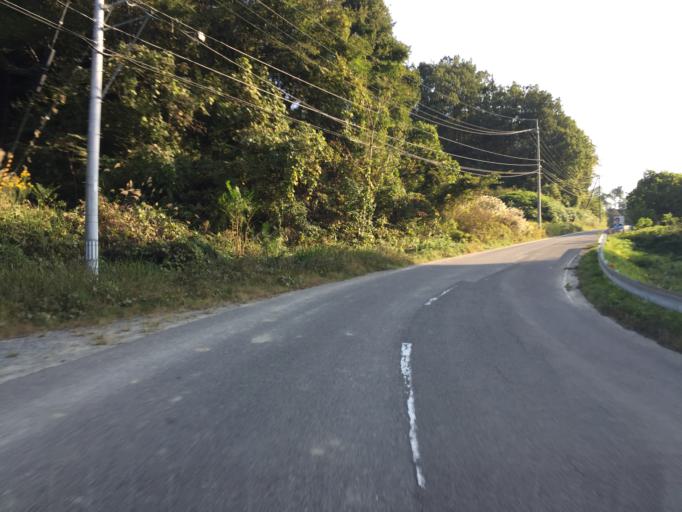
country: JP
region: Fukushima
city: Nihommatsu
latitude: 37.6379
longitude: 140.5556
